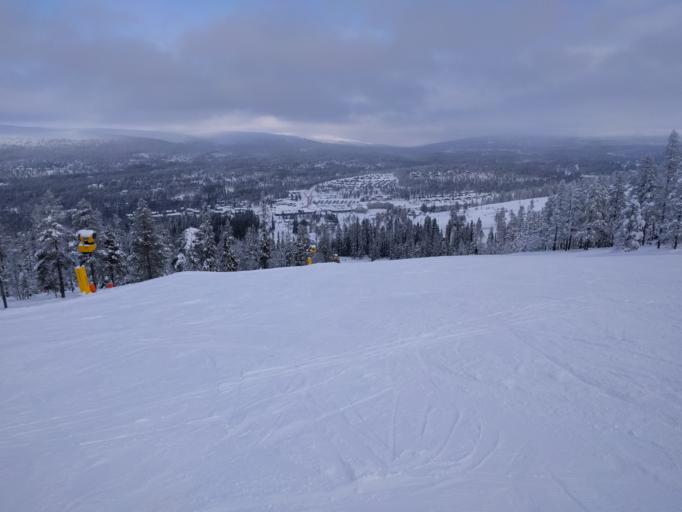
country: NO
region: Hedmark
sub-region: Trysil
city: Innbygda
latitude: 61.1704
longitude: 12.9551
